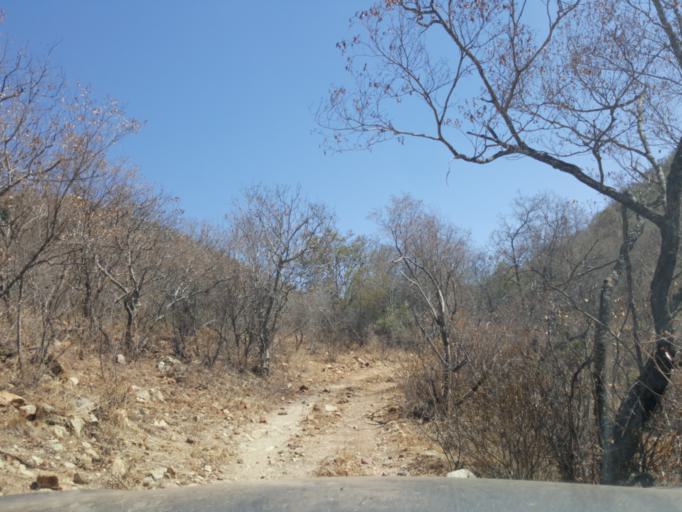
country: BW
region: South East
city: Lobatse
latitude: -25.1549
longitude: 25.6727
